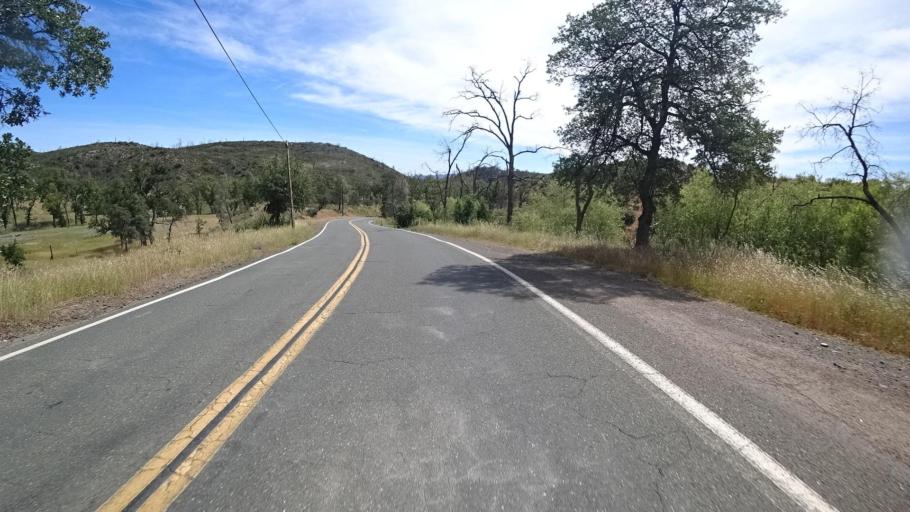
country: US
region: California
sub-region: Lake County
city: Cobb
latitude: 38.8741
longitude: -122.6870
